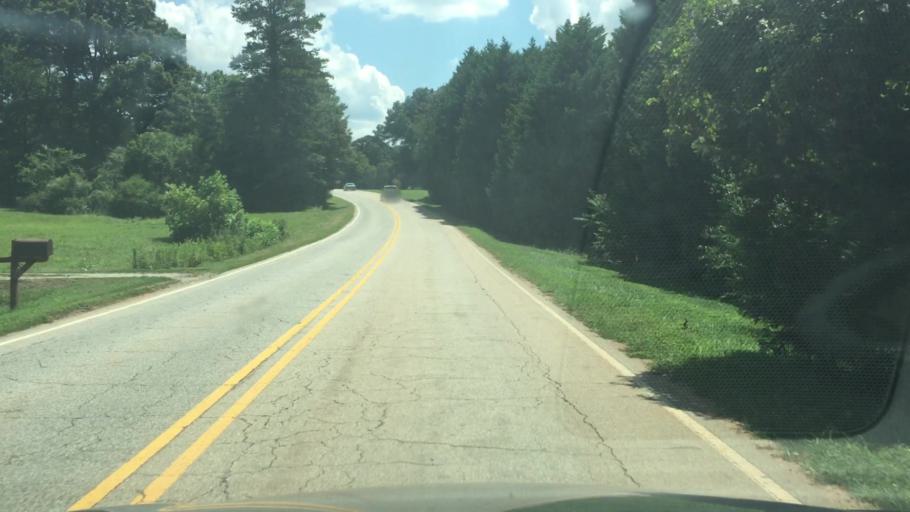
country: US
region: North Carolina
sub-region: Rowan County
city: Landis
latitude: 35.6152
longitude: -80.6529
